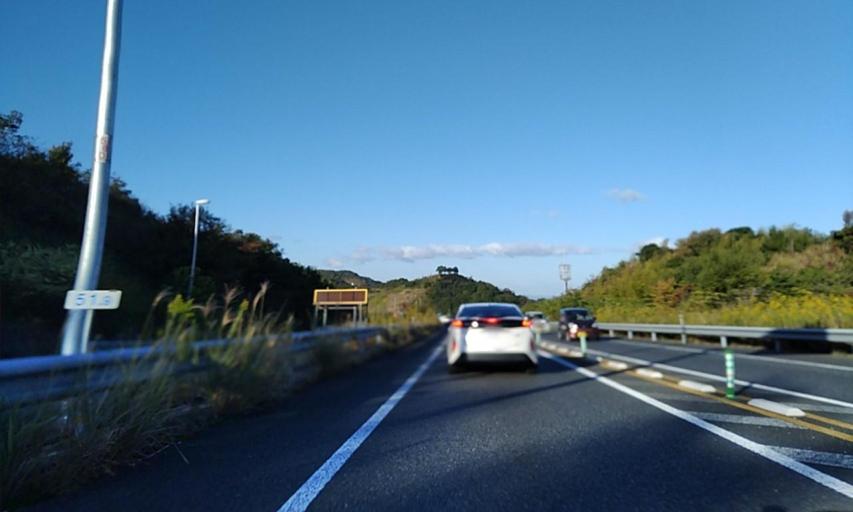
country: JP
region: Wakayama
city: Wakayama-shi
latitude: 34.3338
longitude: 135.2252
